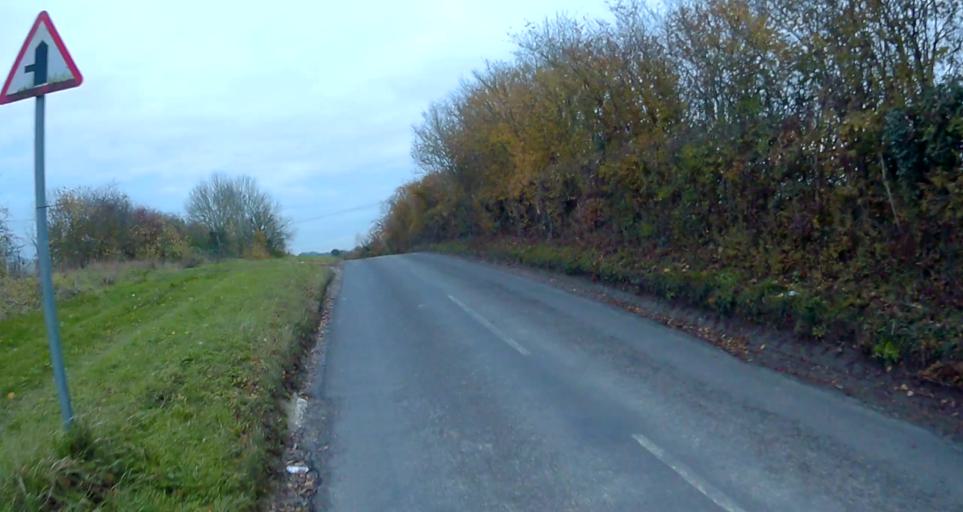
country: GB
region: England
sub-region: Hampshire
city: Odiham
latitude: 51.2463
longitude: -0.9714
